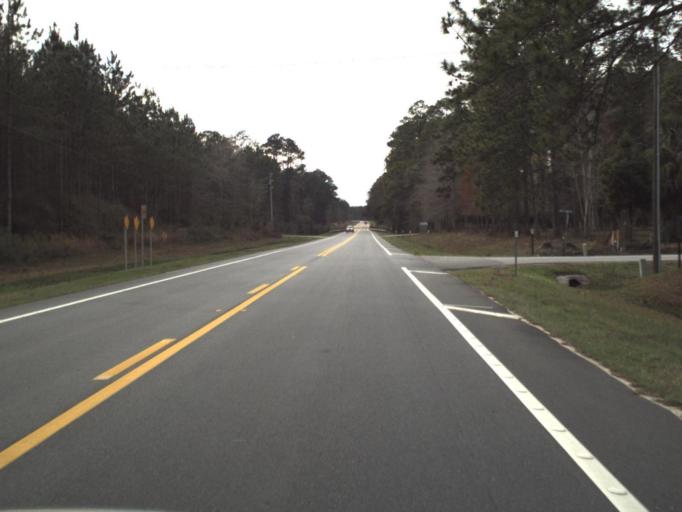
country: US
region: Florida
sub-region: Gulf County
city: Wewahitchka
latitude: 30.1444
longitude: -85.3005
